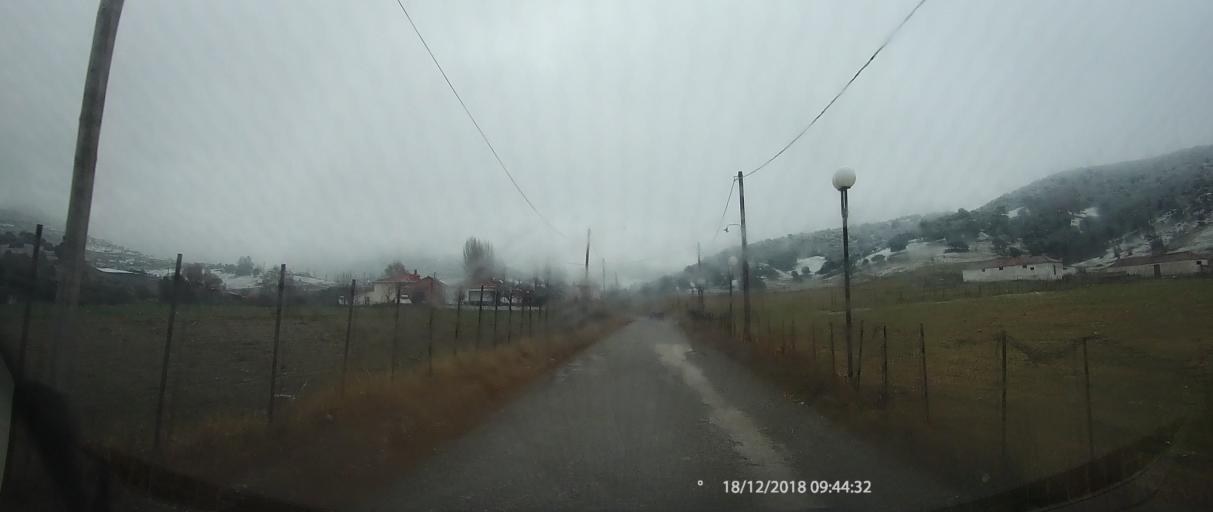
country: GR
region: Thessaly
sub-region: Nomos Larisis
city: Livadi
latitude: 40.0238
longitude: 22.2448
